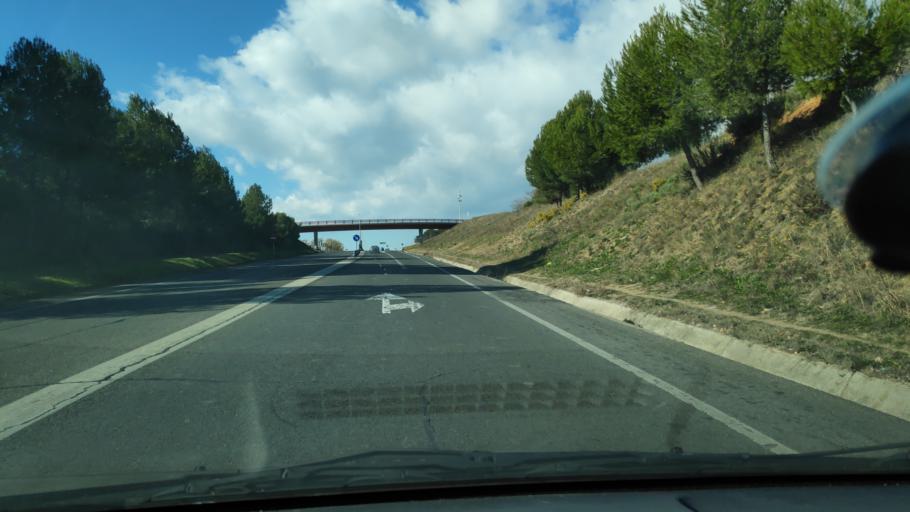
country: ES
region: Catalonia
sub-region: Provincia de Barcelona
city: Terrassa
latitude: 41.5563
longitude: 2.0470
